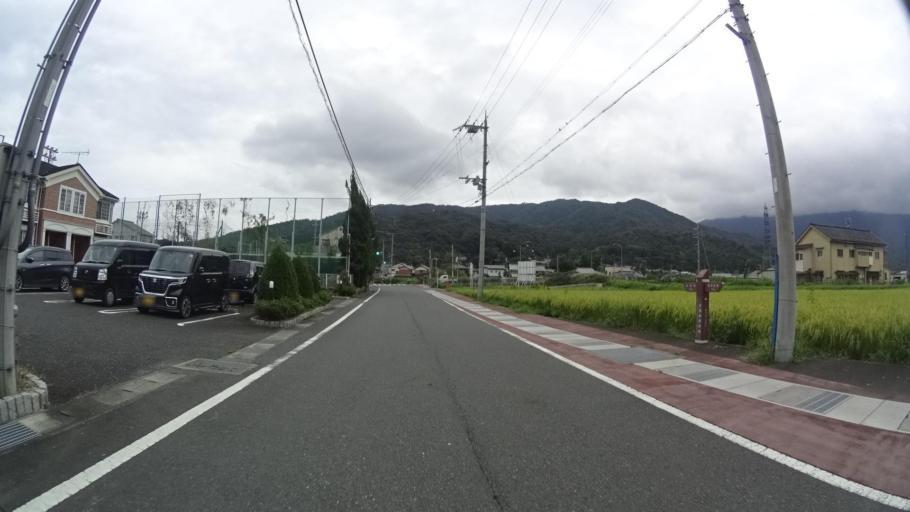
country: JP
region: Kyoto
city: Miyazu
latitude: 35.5282
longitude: 135.1896
